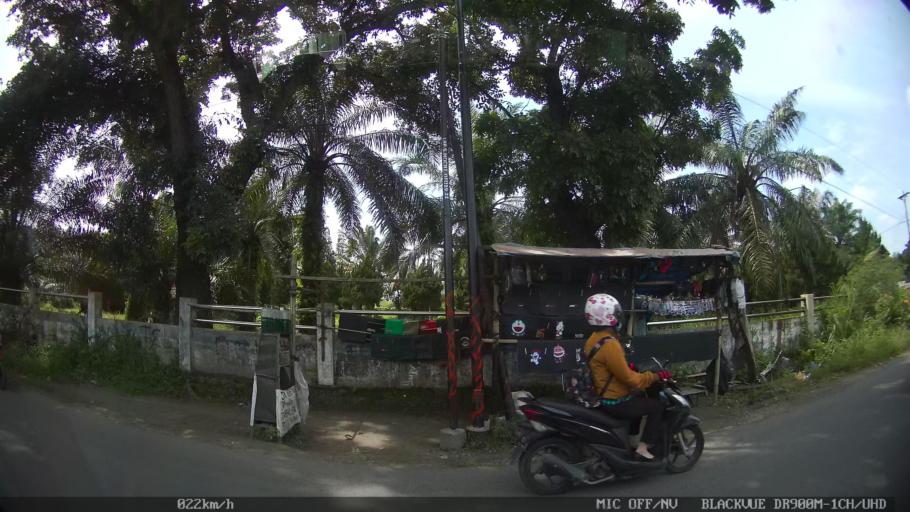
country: ID
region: North Sumatra
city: Medan
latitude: 3.6281
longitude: 98.7144
